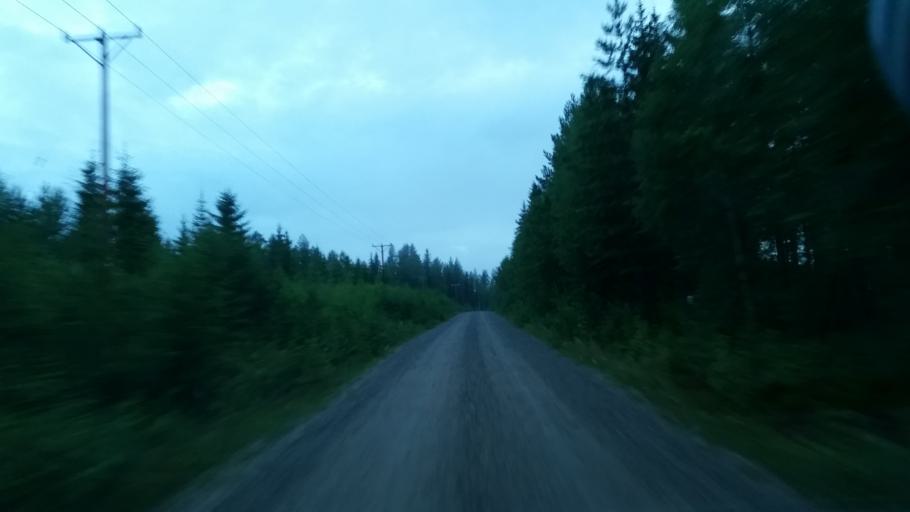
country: SE
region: Gaevleborg
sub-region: Ljusdals Kommun
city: Farila
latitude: 61.9161
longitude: 15.8262
